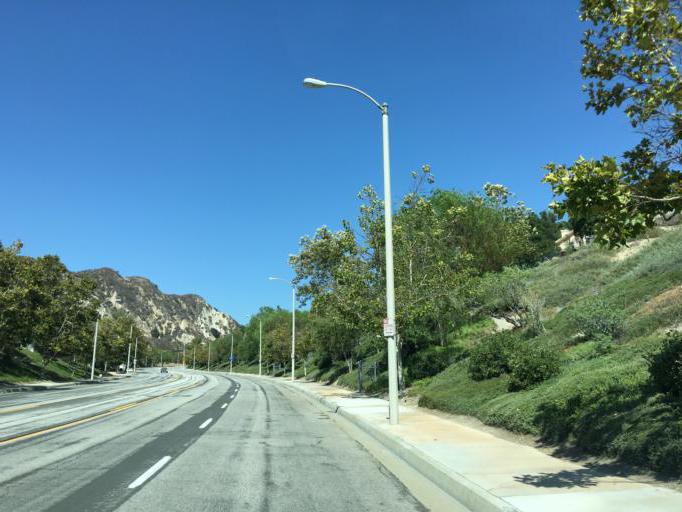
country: US
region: California
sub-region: Los Angeles County
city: Santa Clarita
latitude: 34.3827
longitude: -118.5864
